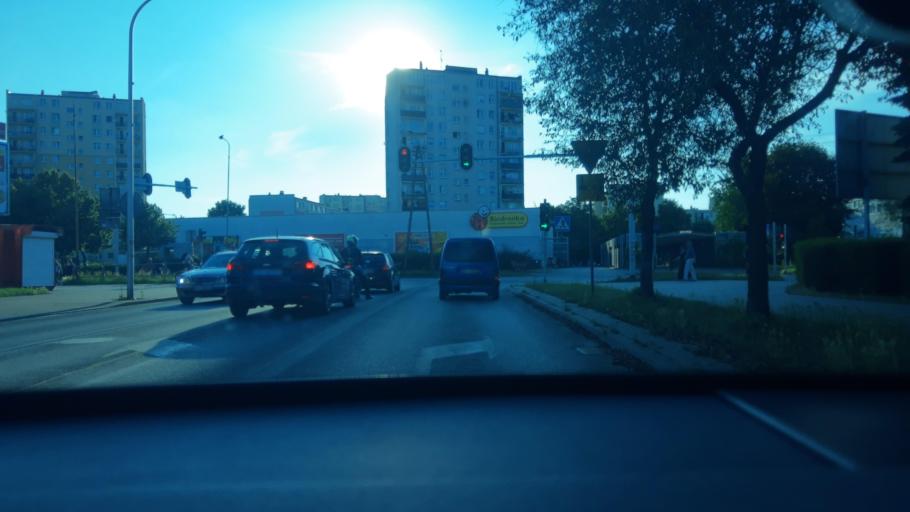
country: PL
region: Lodz Voivodeship
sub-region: Powiat sieradzki
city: Sieradz
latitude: 51.5907
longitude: 18.7266
